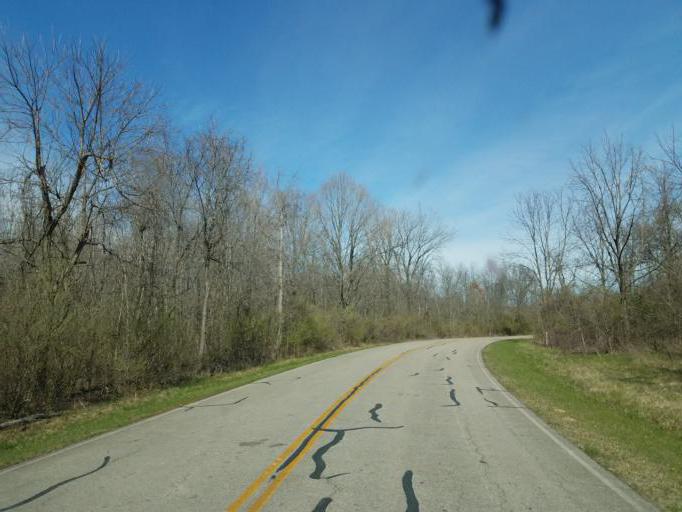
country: US
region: Ohio
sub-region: Delaware County
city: Delaware
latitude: 40.3745
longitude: -83.0615
